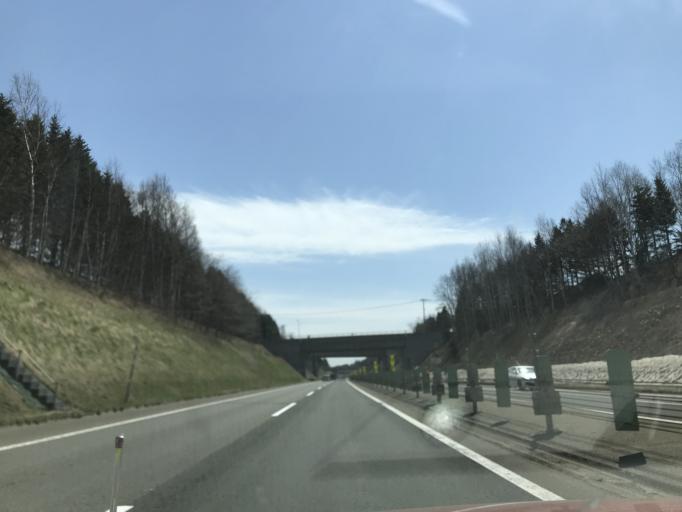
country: JP
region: Hokkaido
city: Ebetsu
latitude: 43.0879
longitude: 141.5130
